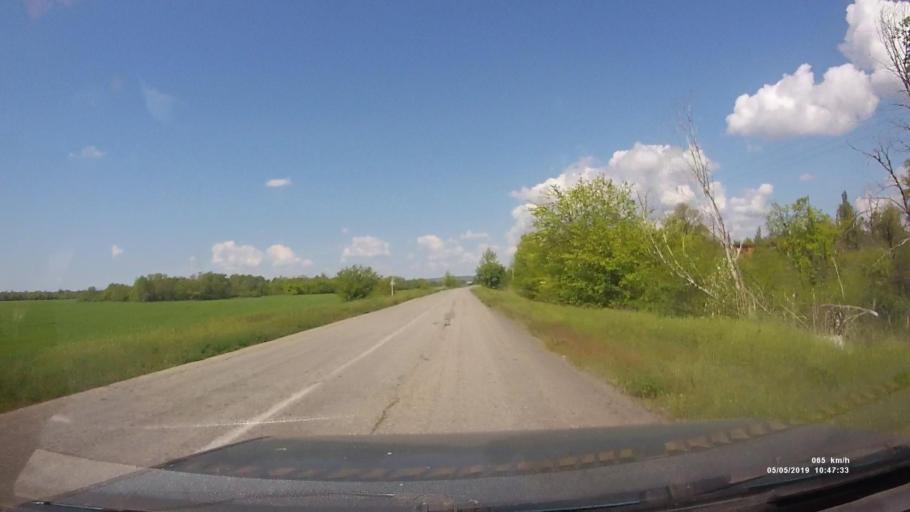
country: RU
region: Rostov
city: Ust'-Donetskiy
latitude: 47.6389
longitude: 40.8312
